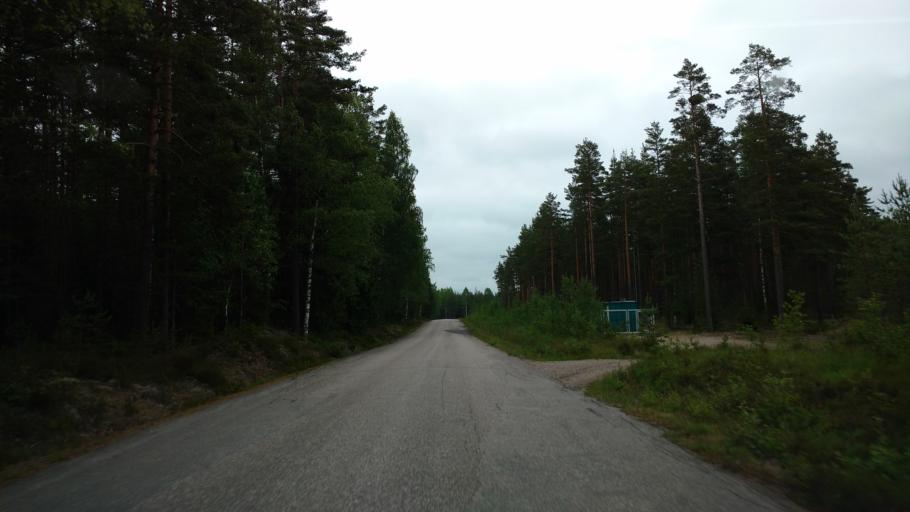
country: FI
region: Varsinais-Suomi
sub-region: Salo
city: Kiikala
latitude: 60.4579
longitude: 23.6390
